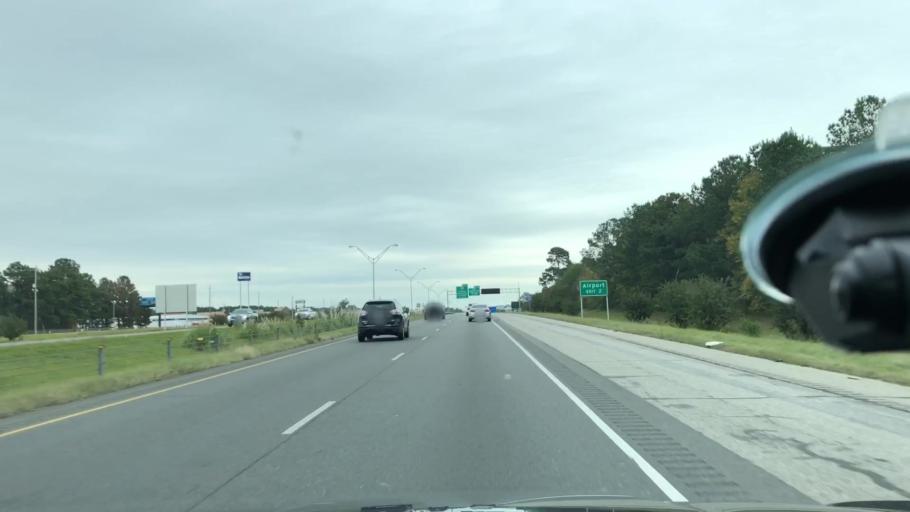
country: US
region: Arkansas
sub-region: Miller County
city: Texarkana
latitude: 33.4723
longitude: -94.0235
